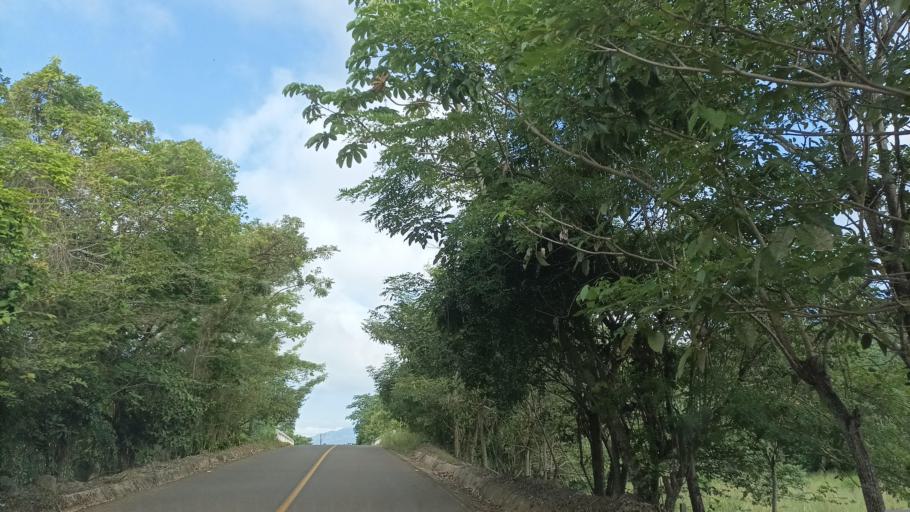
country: MX
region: Veracruz
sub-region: Pajapan
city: Pajapan
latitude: 18.1781
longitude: -94.6718
